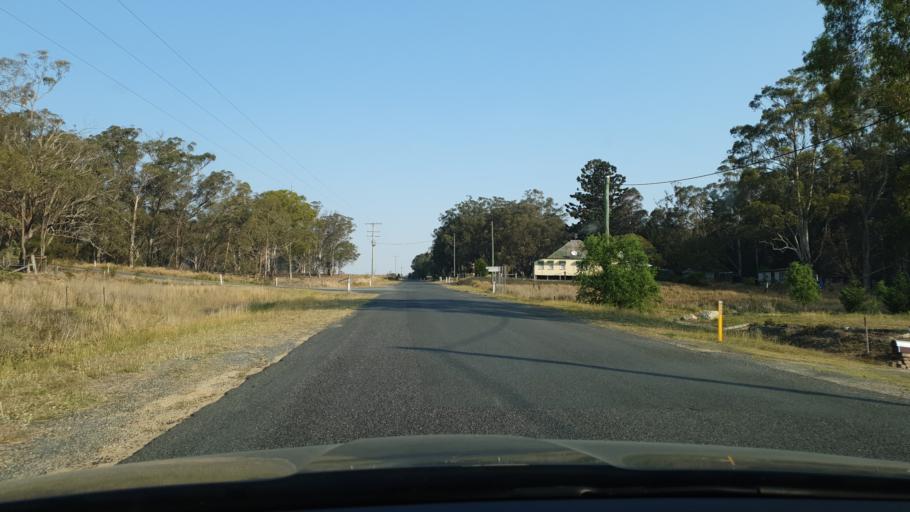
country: AU
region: New South Wales
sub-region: Tenterfield Municipality
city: Carrolls Creek
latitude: -28.6894
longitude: 152.0863
